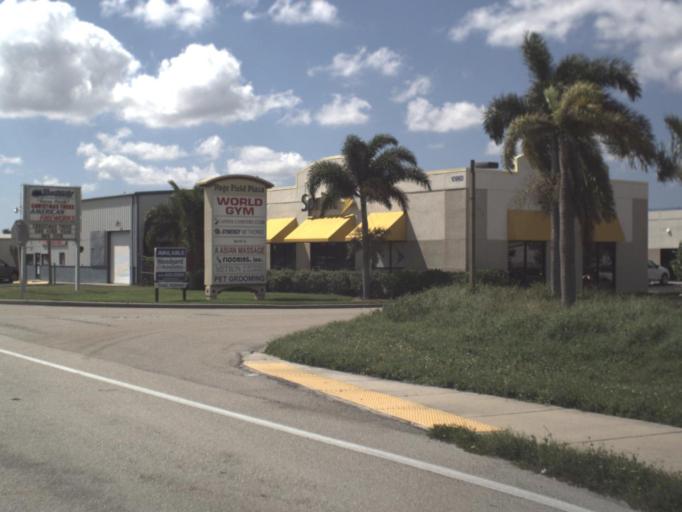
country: US
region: Florida
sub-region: Lee County
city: Pine Manor
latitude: 26.5805
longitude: -81.8720
